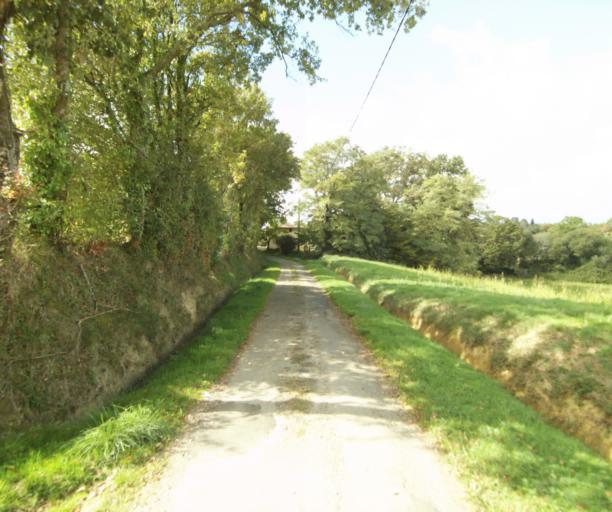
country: FR
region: Midi-Pyrenees
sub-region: Departement du Gers
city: Cazaubon
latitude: 43.8523
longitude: -0.0273
